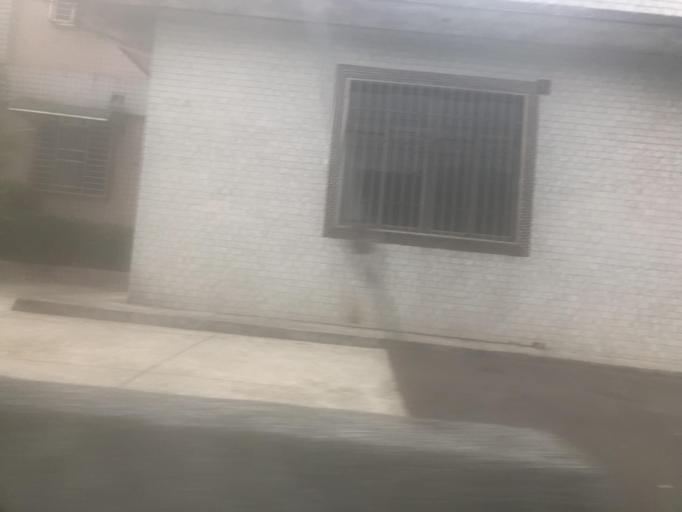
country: TW
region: Taiwan
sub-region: Keelung
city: Keelung
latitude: 25.1655
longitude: 121.6628
